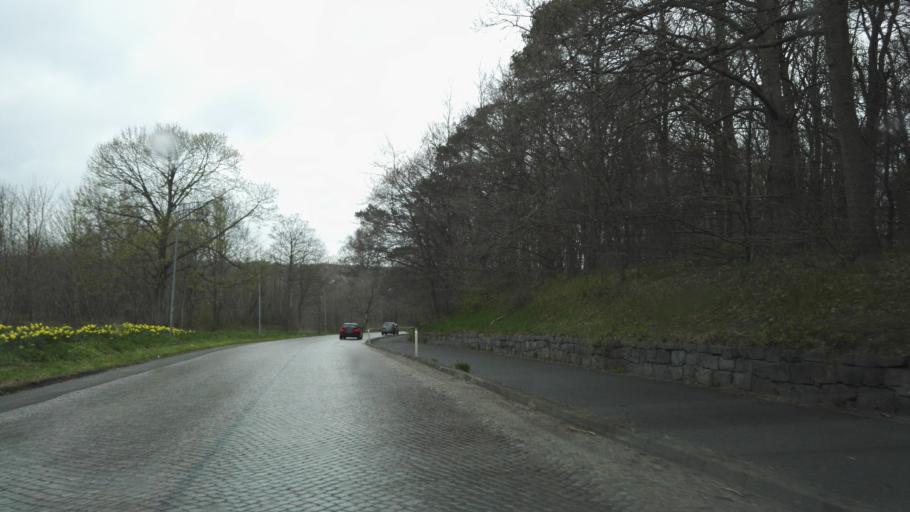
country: SE
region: Skane
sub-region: Simrishamns Kommun
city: Simrishamn
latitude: 55.5670
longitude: 14.3347
